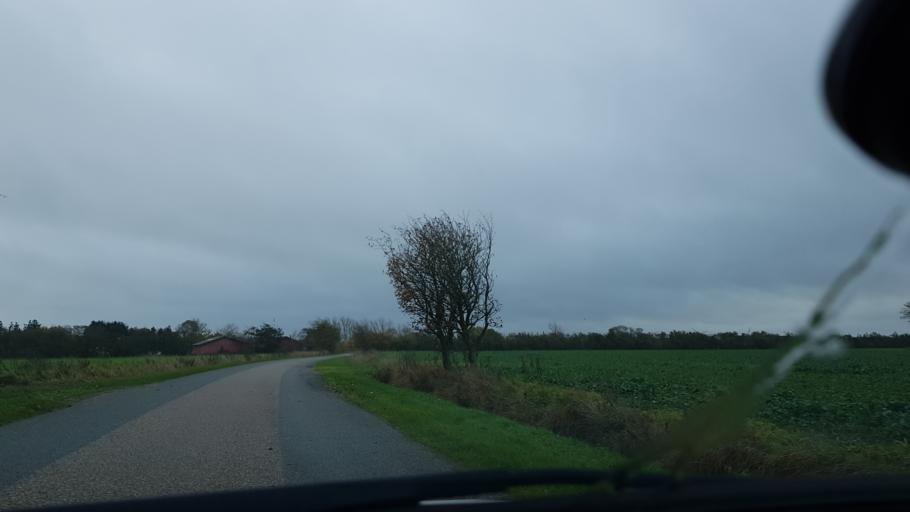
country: DK
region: South Denmark
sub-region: Tonder Kommune
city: Sherrebek
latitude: 55.2142
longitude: 8.7987
